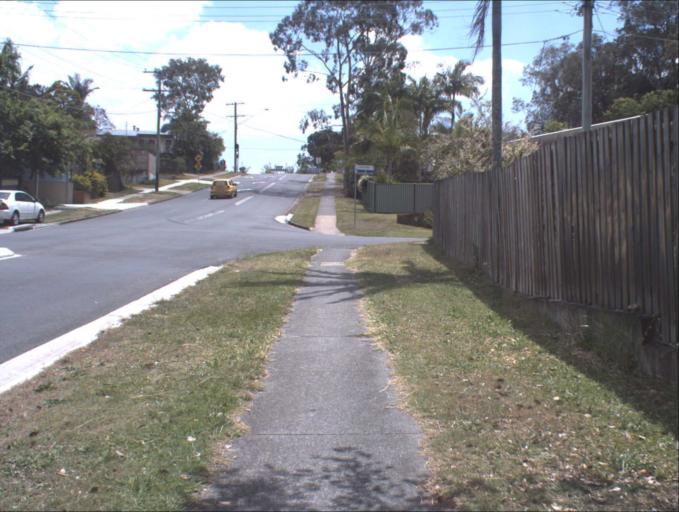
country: AU
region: Queensland
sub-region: Logan
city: Springwood
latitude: -27.6185
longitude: 153.1329
